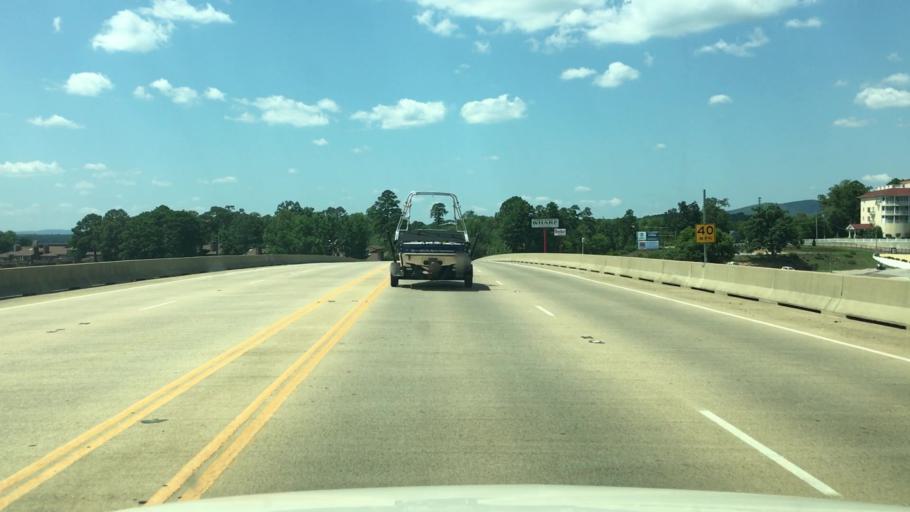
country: US
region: Arkansas
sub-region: Garland County
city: Lake Hamilton
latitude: 34.4328
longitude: -93.0872
